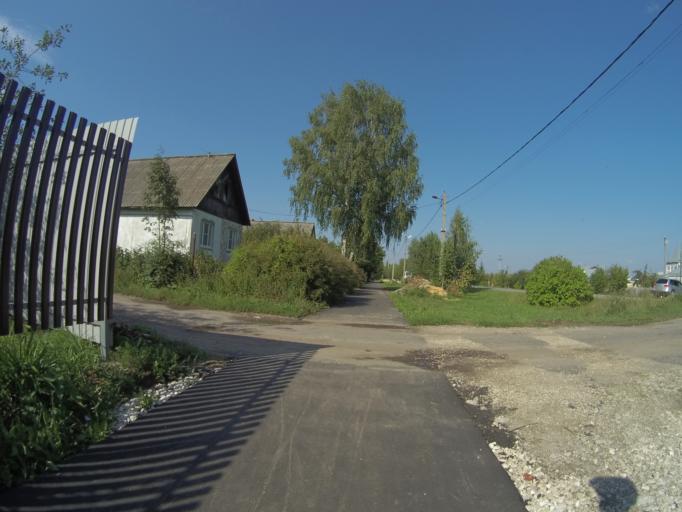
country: RU
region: Vladimir
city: Bogolyubovo
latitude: 56.2693
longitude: 40.5261
